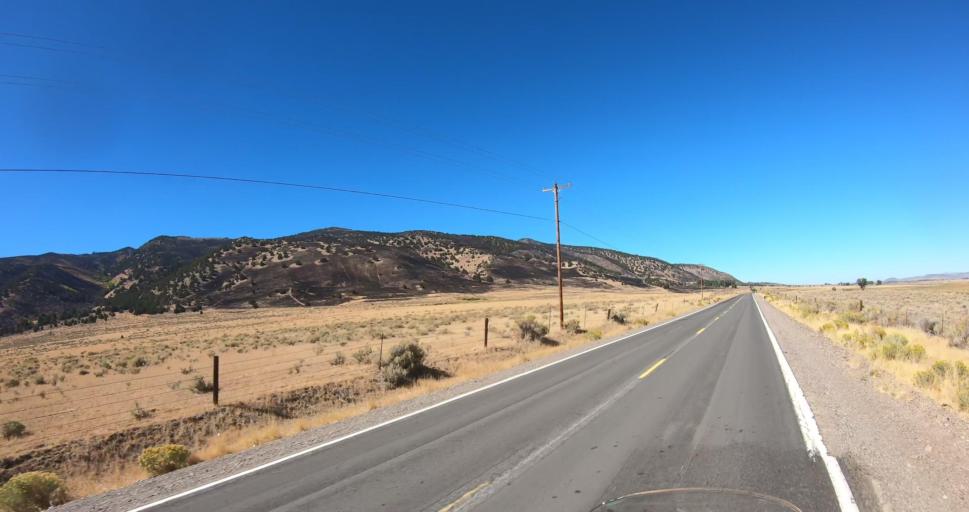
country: US
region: Oregon
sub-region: Lake County
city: Lakeview
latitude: 42.6286
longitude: -120.5110
